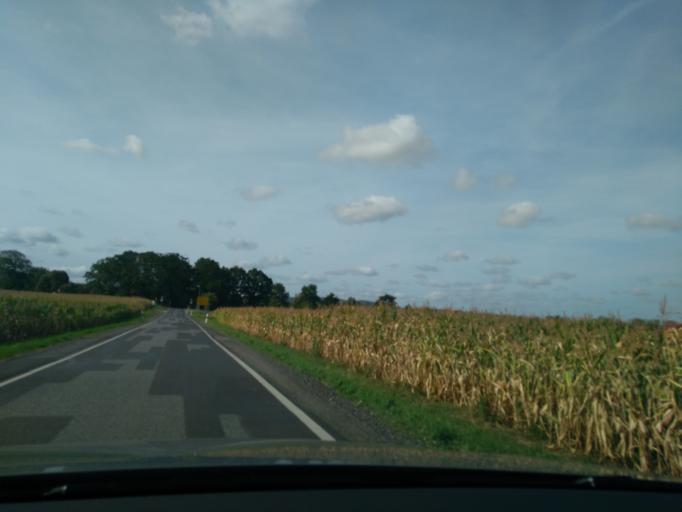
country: DE
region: Saxony
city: Kubschutz
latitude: 51.1561
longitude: 14.4641
